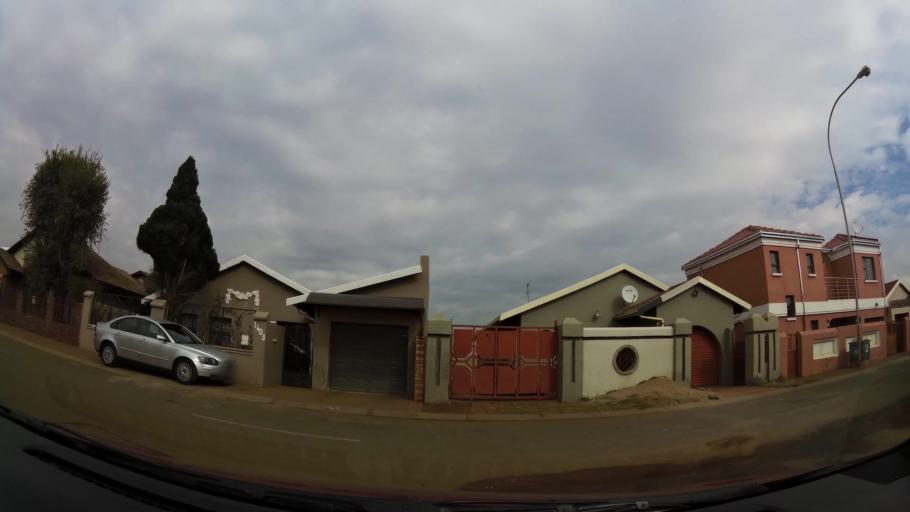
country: ZA
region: Gauteng
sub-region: City of Johannesburg Metropolitan Municipality
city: Soweto
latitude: -26.2706
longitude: 27.8262
